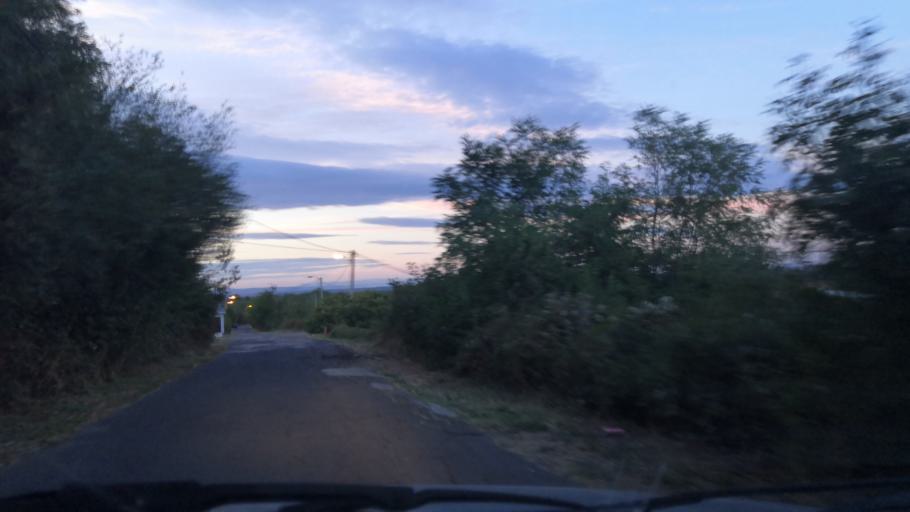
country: RO
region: Mehedinti
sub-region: Comuna Gogosu
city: Balta Verde
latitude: 44.3084
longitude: 22.5492
